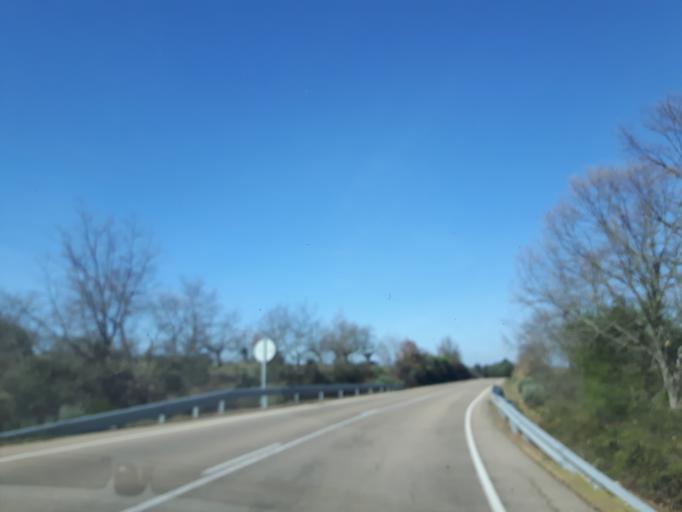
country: ES
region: Castille and Leon
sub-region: Provincia de Salamanca
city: Encinasola de los Comendadores
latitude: 40.9940
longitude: -6.5457
